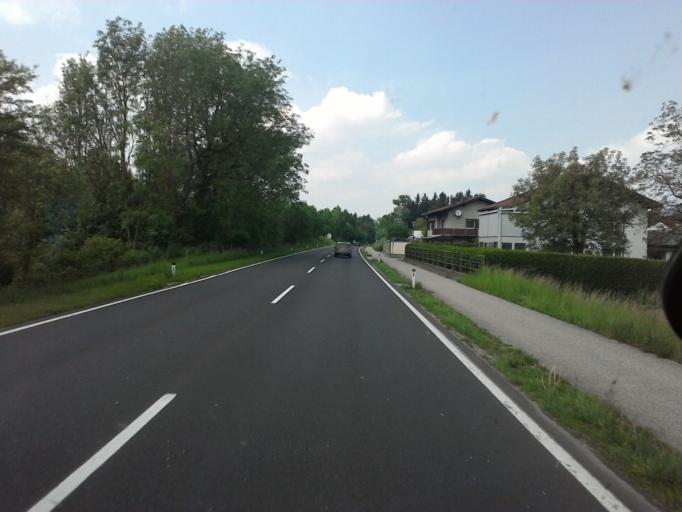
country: AT
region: Upper Austria
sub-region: Wels-Land
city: Sattledt
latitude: 48.0898
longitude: 14.0430
